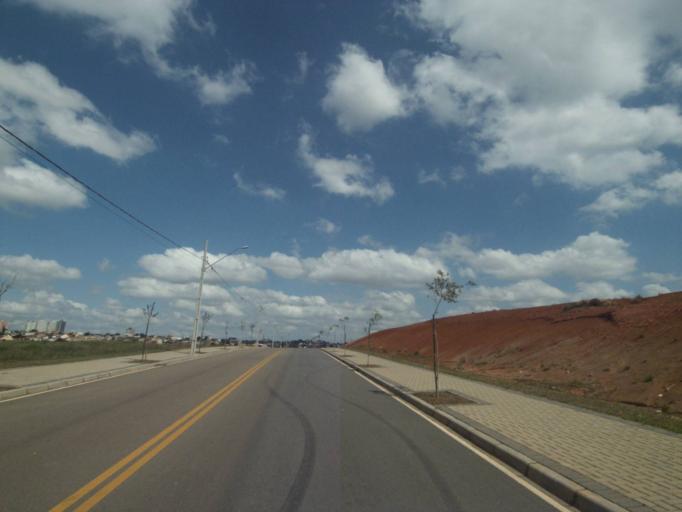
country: BR
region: Parana
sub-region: Curitiba
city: Curitiba
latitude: -25.5066
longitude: -49.3094
